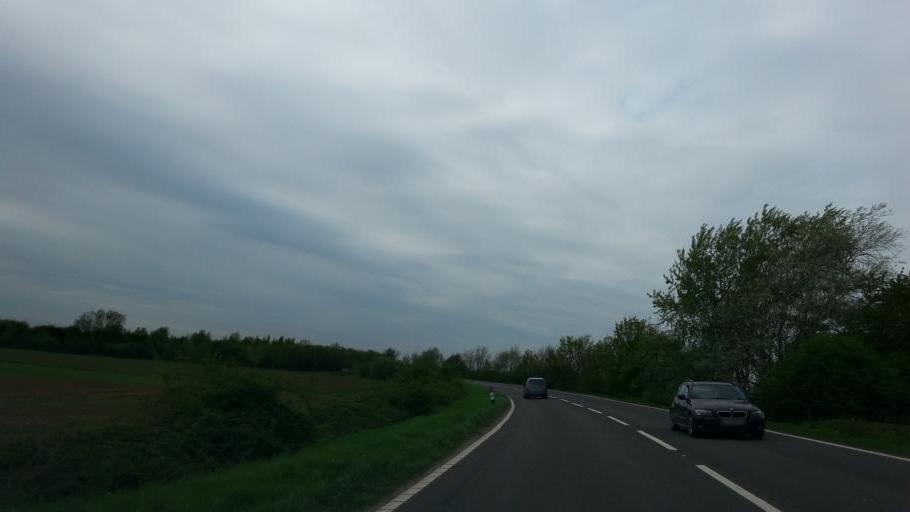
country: GB
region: England
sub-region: Cambridgeshire
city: March
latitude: 52.5188
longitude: 0.0909
